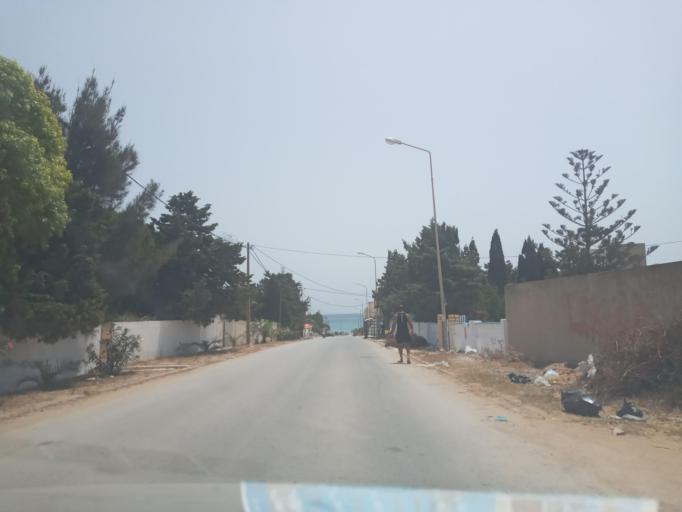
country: TN
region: Nabul
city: El Haouaria
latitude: 37.0362
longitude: 11.0555
